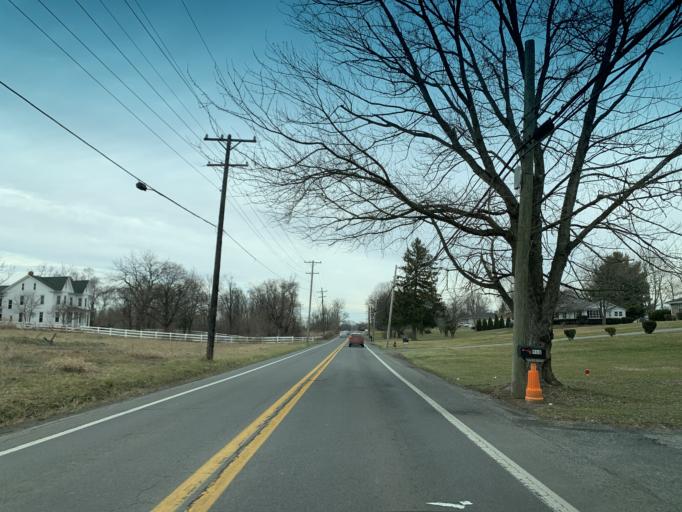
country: US
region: West Virginia
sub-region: Berkeley County
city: Martinsburg
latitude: 39.4865
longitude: -77.9464
